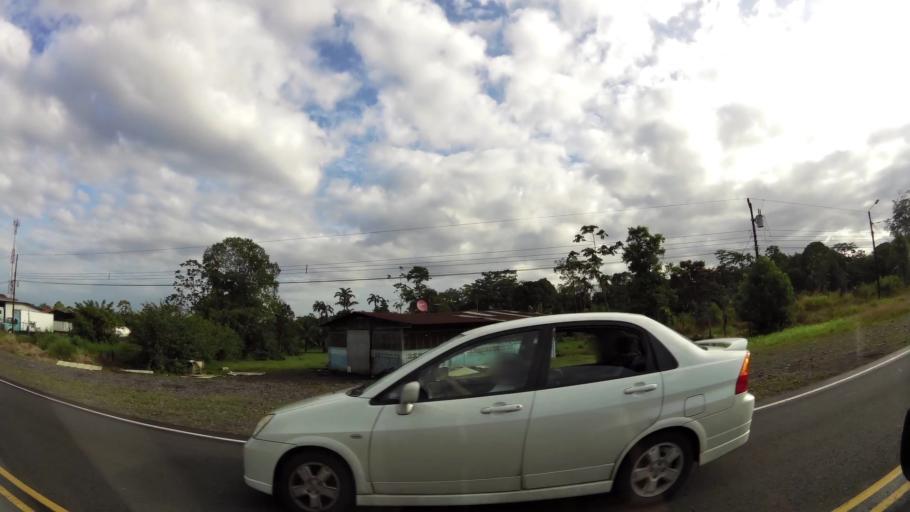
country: CR
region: Limon
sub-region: Canton de Pococi
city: Guapiles
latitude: 10.2105
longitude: -83.8355
